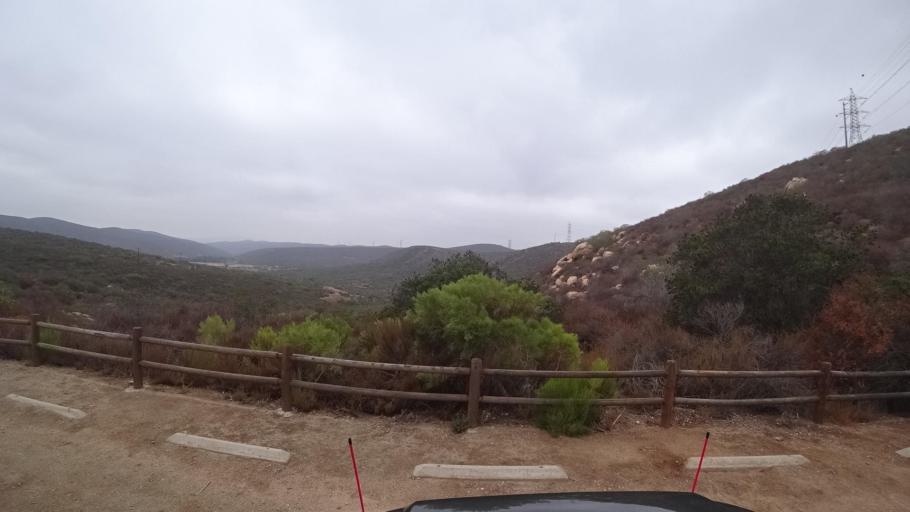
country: US
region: California
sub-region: San Diego County
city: Poway
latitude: 32.9409
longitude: -116.9807
